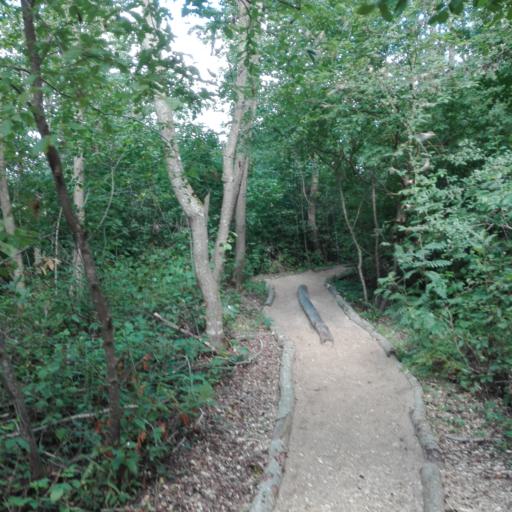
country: LT
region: Panevezys
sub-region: Birzai
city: Birzai
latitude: 56.2333
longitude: 24.7839
